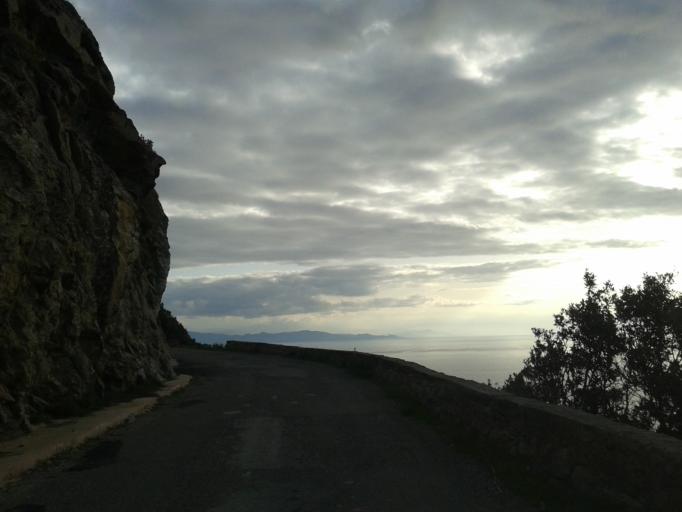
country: FR
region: Corsica
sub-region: Departement de la Haute-Corse
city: Brando
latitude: 42.8973
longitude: 9.3242
